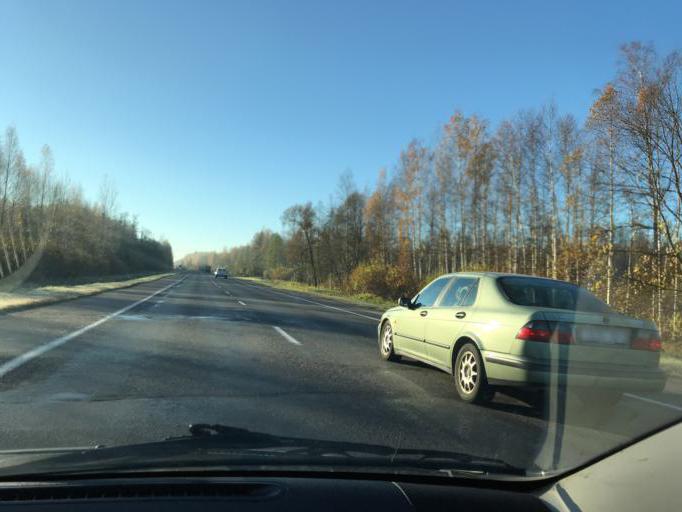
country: BY
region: Vitebsk
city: Vitebsk
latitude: 54.9598
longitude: 30.3563
